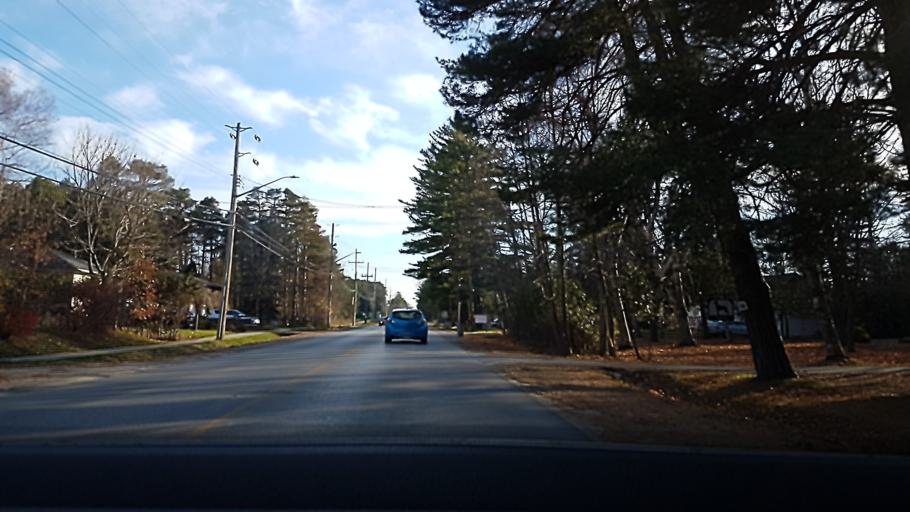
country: CA
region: Ontario
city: Keswick
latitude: 44.3209
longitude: -79.5411
